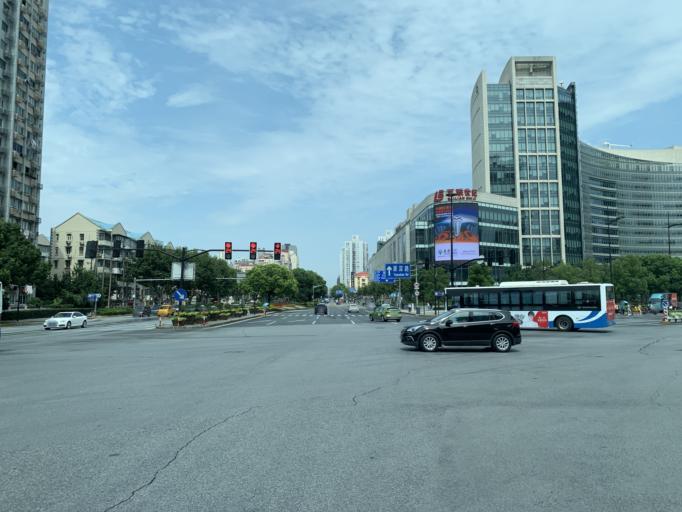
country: CN
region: Shanghai Shi
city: Pudong
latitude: 31.2319
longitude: 121.5206
